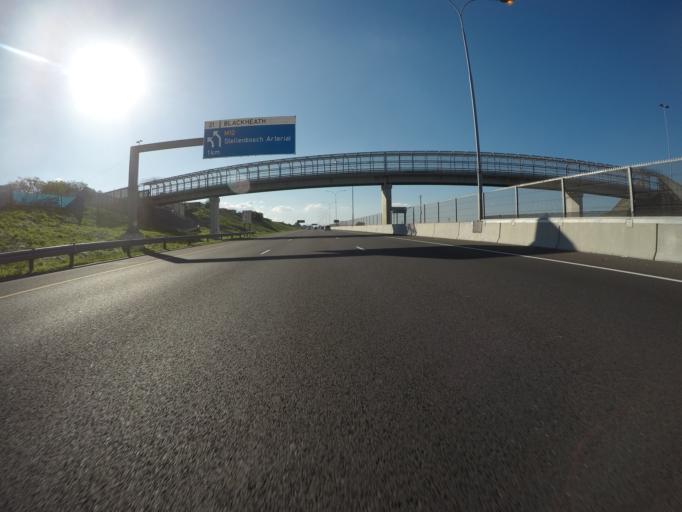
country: ZA
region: Western Cape
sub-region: City of Cape Town
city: Kraaifontein
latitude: -33.9683
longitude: 18.6545
